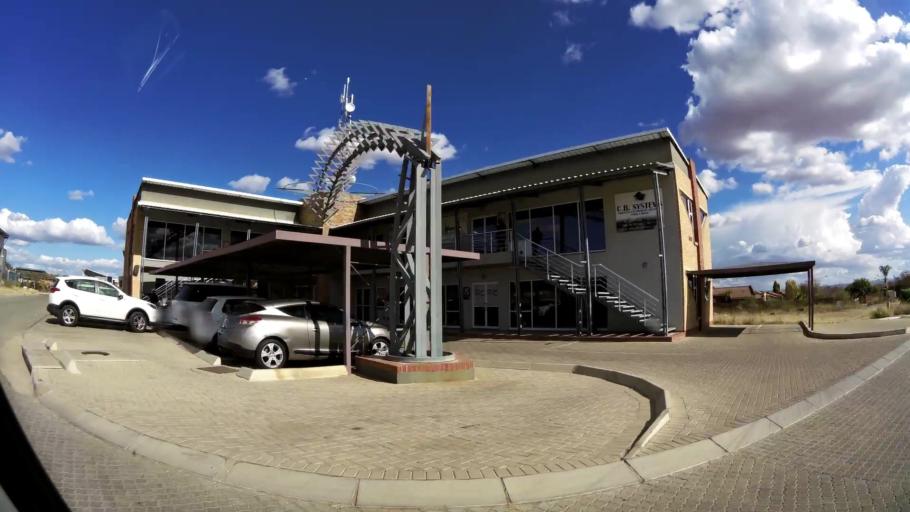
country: ZA
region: Limpopo
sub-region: Capricorn District Municipality
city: Polokwane
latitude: -23.8869
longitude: 29.4734
